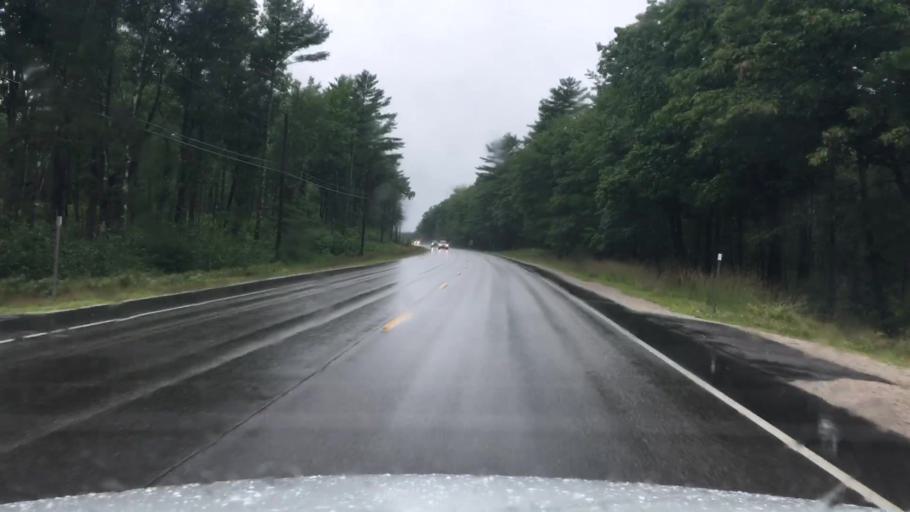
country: US
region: Maine
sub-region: Oxford County
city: Fryeburg
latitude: 43.9990
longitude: -71.0103
